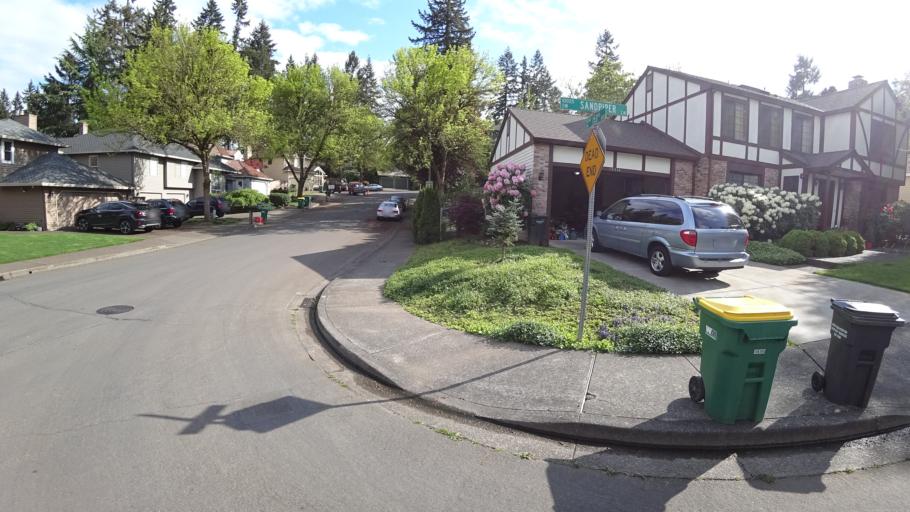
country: US
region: Oregon
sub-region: Washington County
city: Beaverton
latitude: 45.4472
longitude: -122.8338
